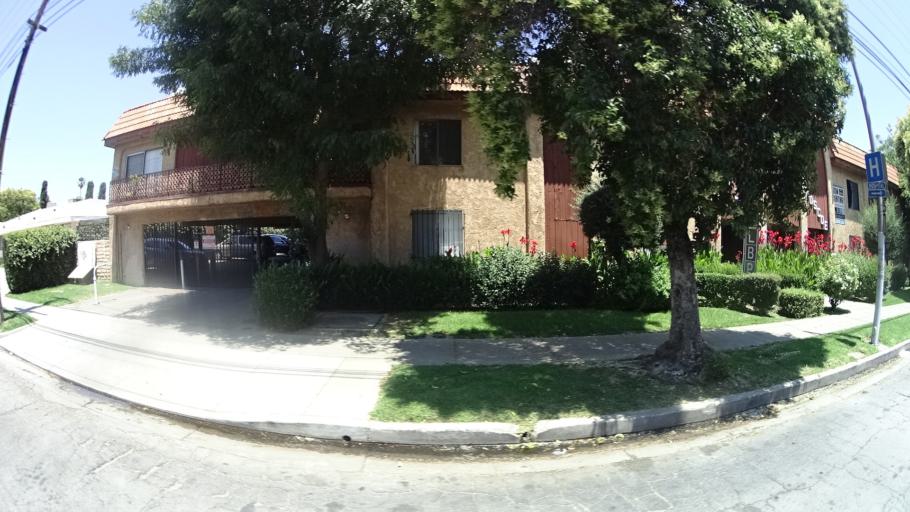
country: US
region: California
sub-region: Los Angeles County
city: Van Nuys
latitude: 34.2216
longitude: -118.4566
